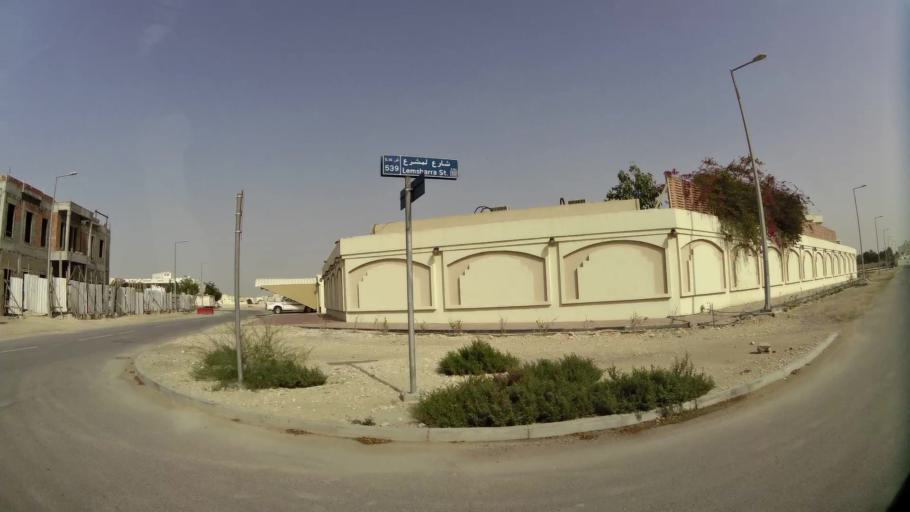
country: QA
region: Baladiyat ar Rayyan
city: Ar Rayyan
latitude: 25.2436
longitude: 51.4394
